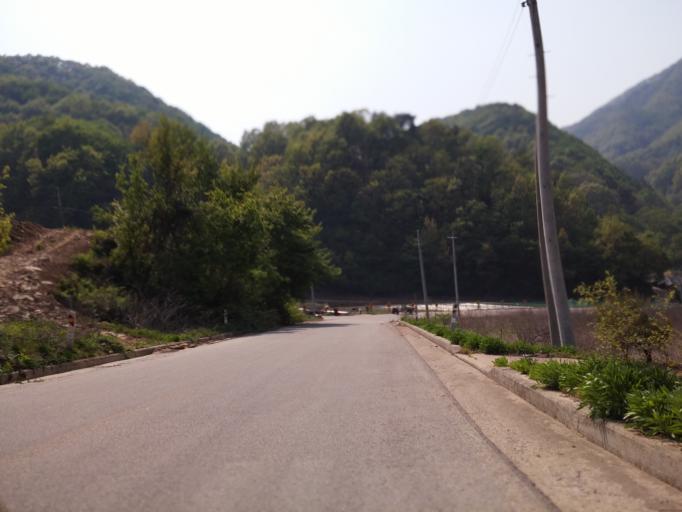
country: KR
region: Chungcheongbuk-do
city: Okcheon
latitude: 36.3901
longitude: 127.6026
